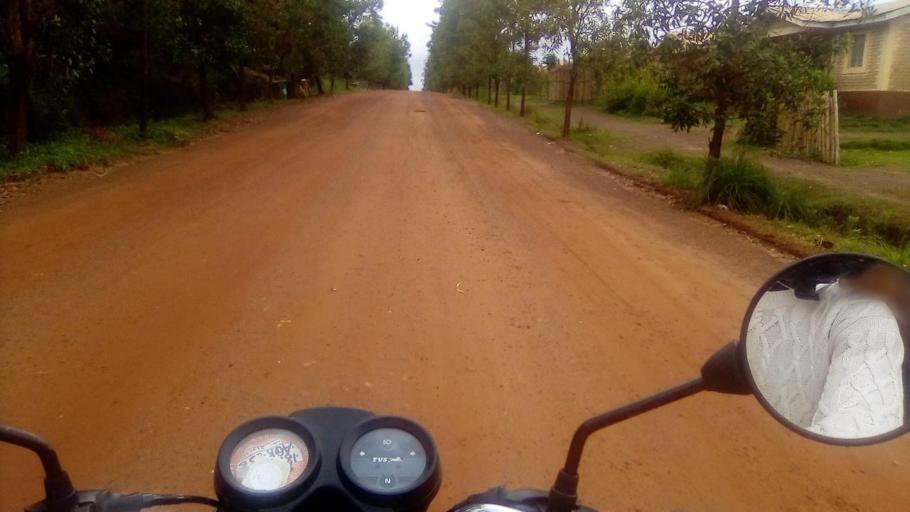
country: SL
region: Southern Province
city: Tongole
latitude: 7.4339
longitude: -11.8456
